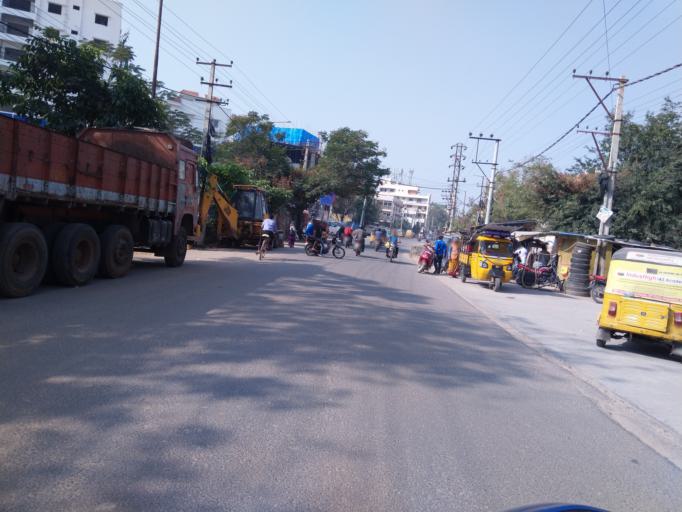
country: IN
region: Telangana
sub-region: Rangareddi
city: Kukatpalli
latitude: 17.4992
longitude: 78.4134
